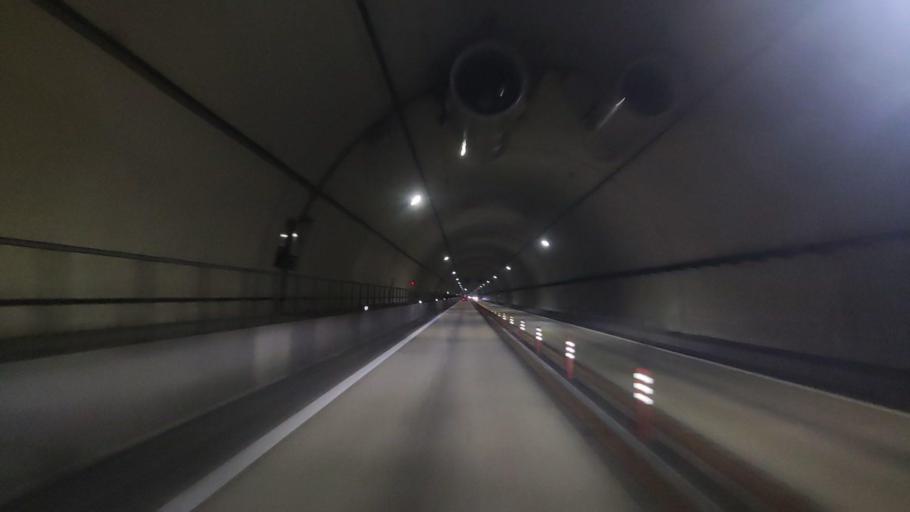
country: JP
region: Wakayama
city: Tanabe
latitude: 33.5675
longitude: 135.4905
